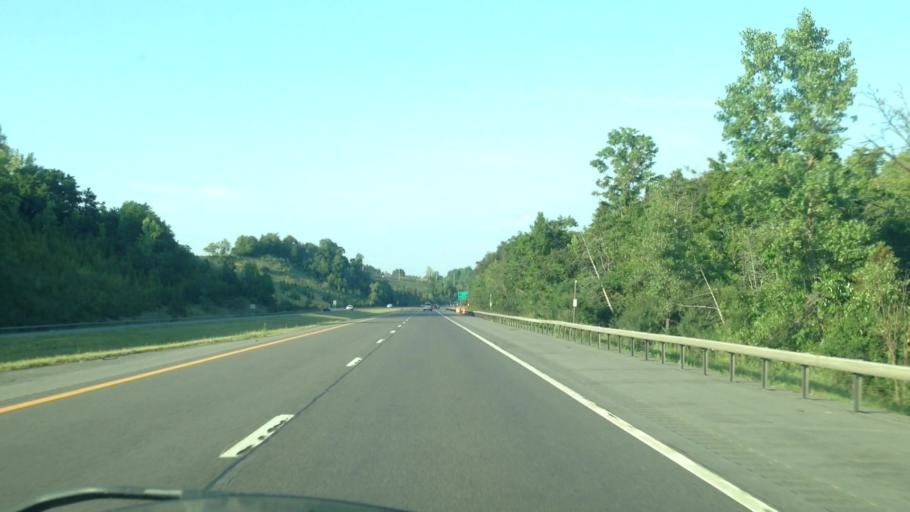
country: US
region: New York
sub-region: Onondaga County
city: East Syracuse
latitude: 43.0063
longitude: -76.0892
